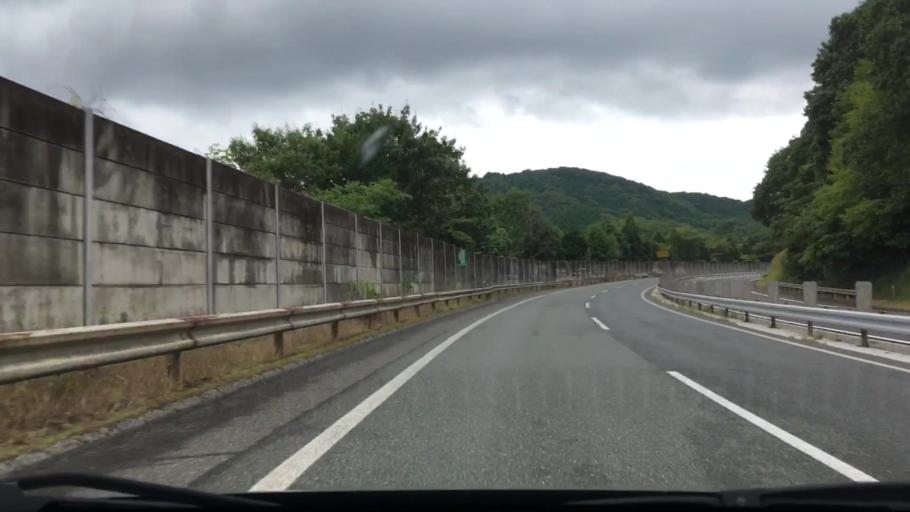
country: JP
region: Okayama
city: Niimi
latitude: 34.9040
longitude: 133.3019
